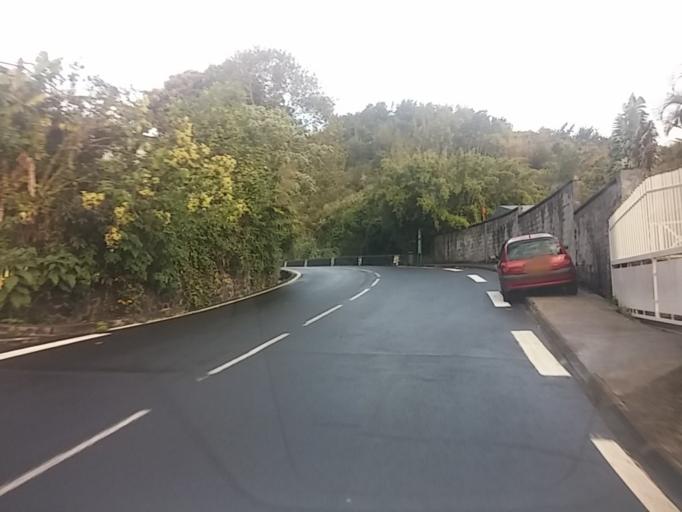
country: RE
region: Reunion
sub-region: Reunion
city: Saint-Denis
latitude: -20.9016
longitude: 55.4195
